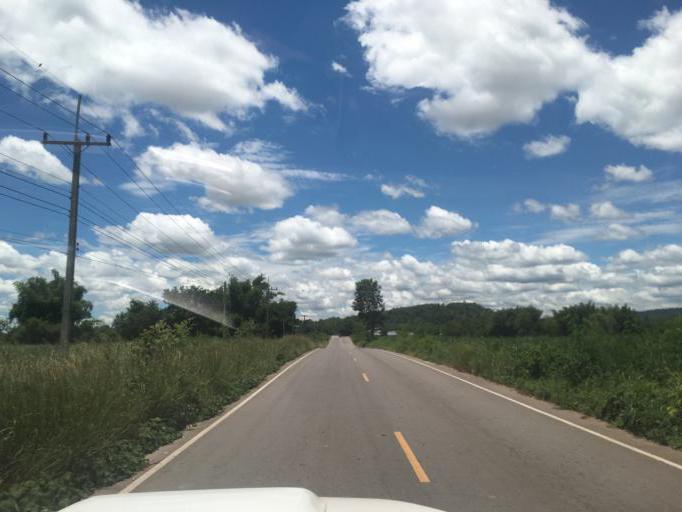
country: TH
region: Changwat Udon Thani
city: Nong Saeng
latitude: 17.2230
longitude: 102.7468
